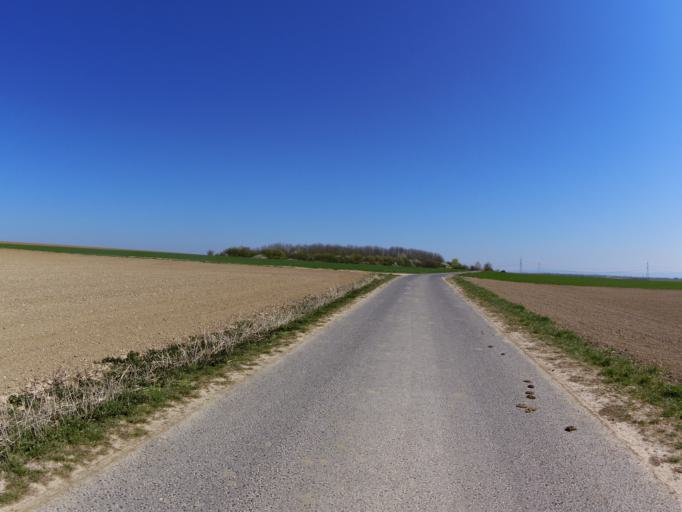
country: DE
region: Bavaria
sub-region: Regierungsbezirk Unterfranken
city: Kurnach
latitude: 49.8361
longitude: 10.0684
